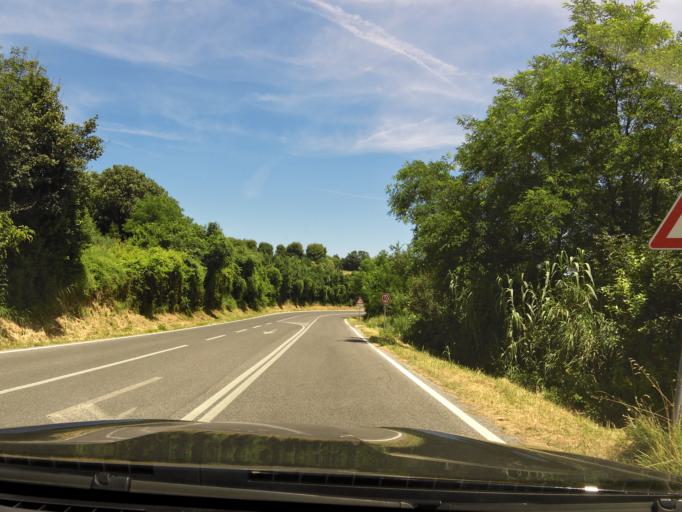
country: IT
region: The Marches
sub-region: Provincia di Ancona
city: Pietra la Croce
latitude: 43.5813
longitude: 13.5603
